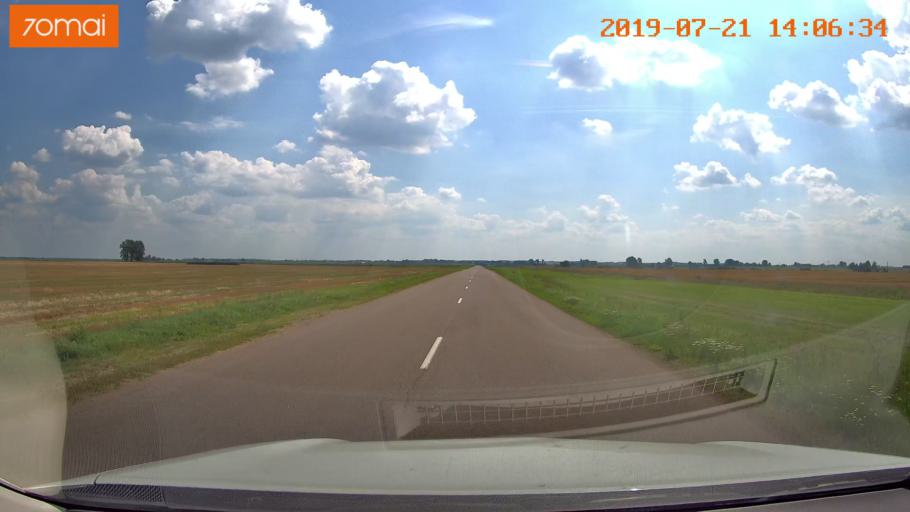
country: BY
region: Grodnenskaya
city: Lyubcha
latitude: 53.6955
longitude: 26.1133
